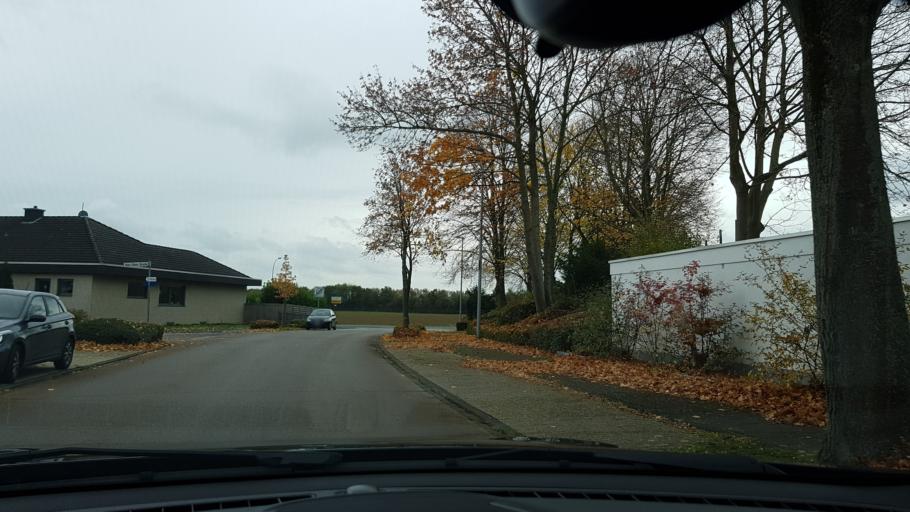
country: DE
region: North Rhine-Westphalia
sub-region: Regierungsbezirk Koln
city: Bedburg
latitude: 51.0024
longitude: 6.5388
